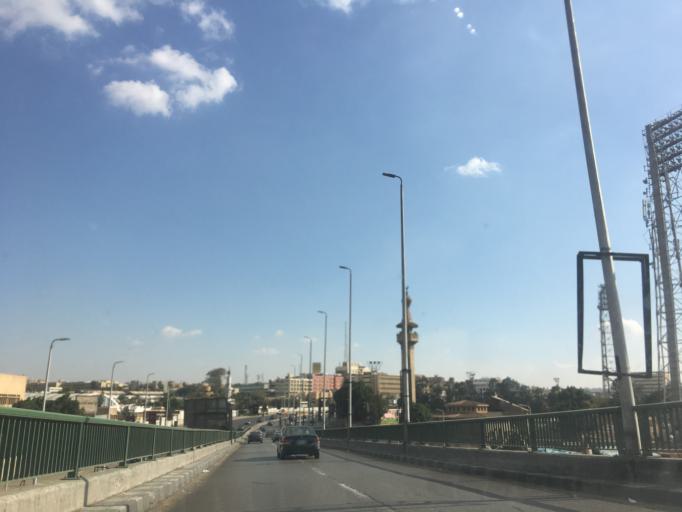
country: EG
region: Muhafazat al Qahirah
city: Cairo
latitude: 30.0573
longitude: 31.3042
